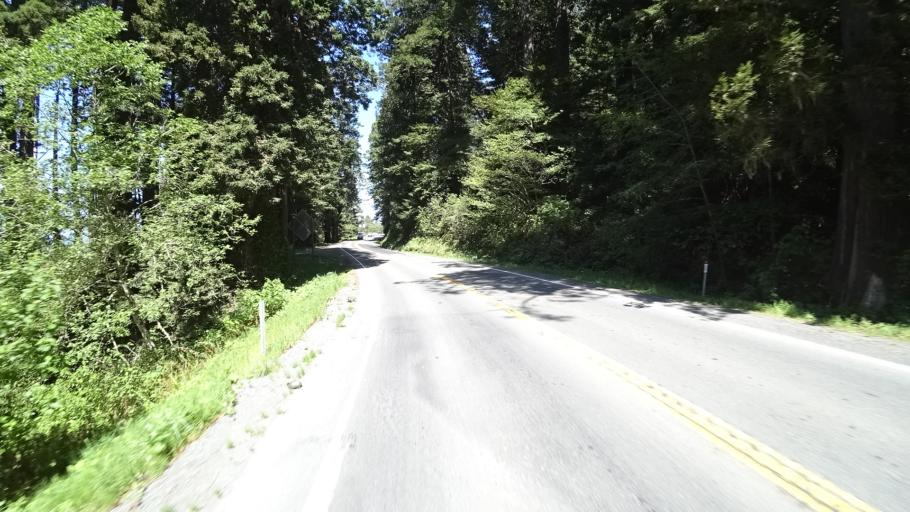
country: US
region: California
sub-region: Humboldt County
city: Westhaven-Moonstone
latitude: 41.1885
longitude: -124.1080
